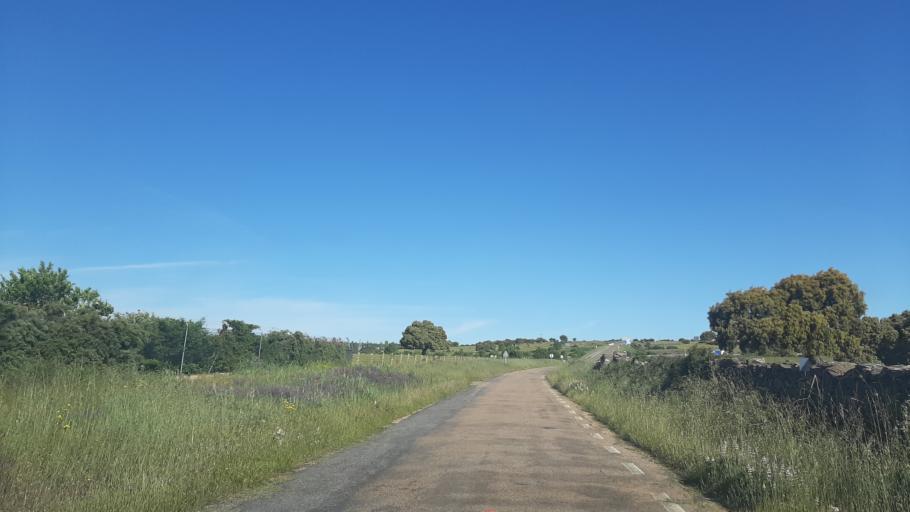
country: ES
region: Castille and Leon
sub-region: Provincia de Salamanca
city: Guijo de Avila
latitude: 40.5380
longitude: -5.6573
